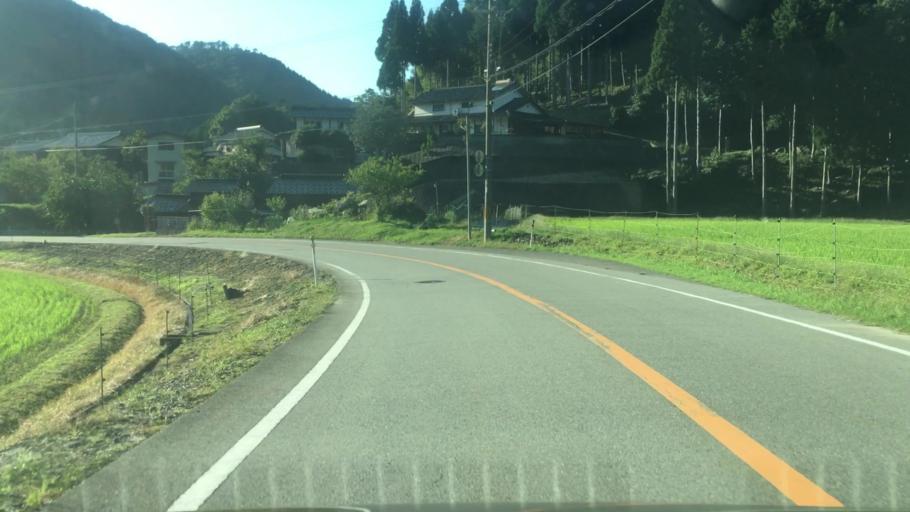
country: JP
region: Hyogo
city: Toyooka
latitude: 35.6214
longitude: 134.8665
